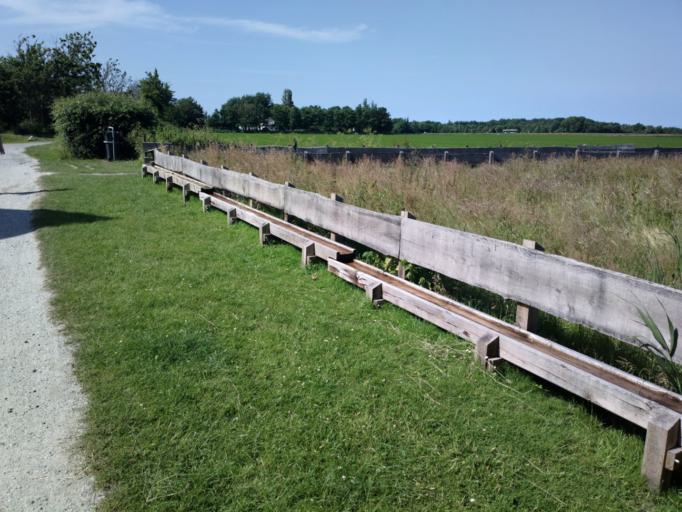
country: NL
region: North Holland
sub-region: Gemeente Texel
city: Den Burg
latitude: 53.0398
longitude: 4.8310
